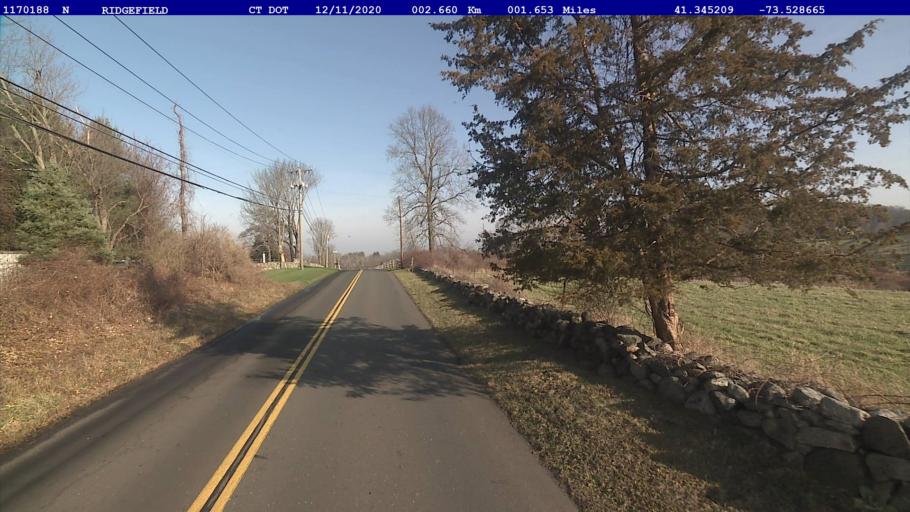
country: US
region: New York
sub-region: Putnam County
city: Peach Lake
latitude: 41.3452
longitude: -73.5287
